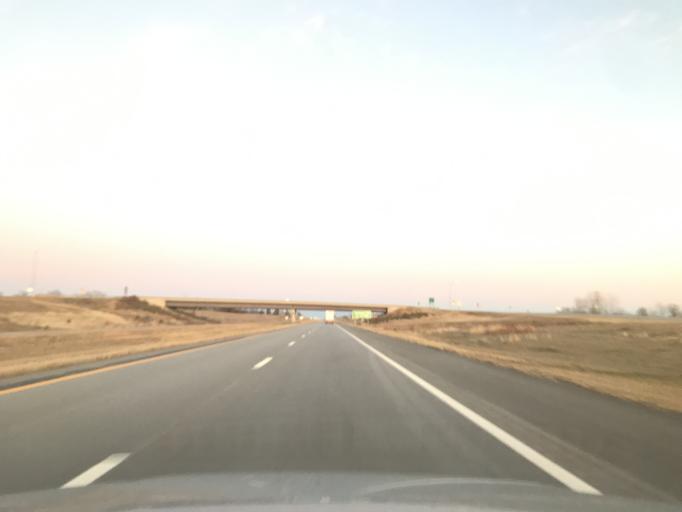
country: US
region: Missouri
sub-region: Marion County
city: Hannibal
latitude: 39.7133
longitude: -91.4486
